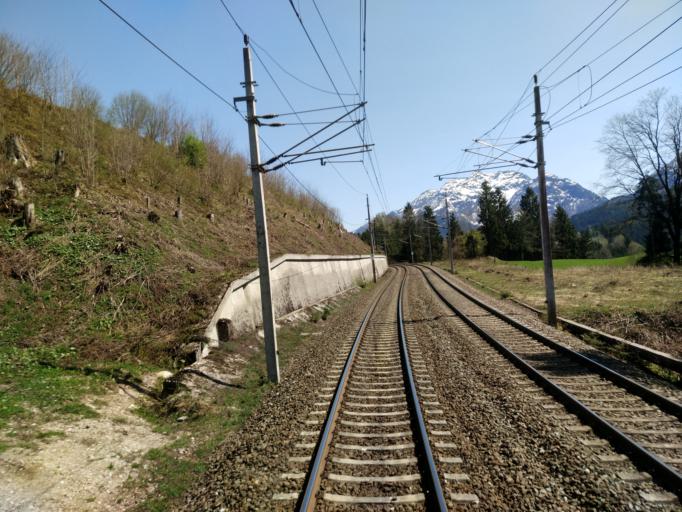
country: AT
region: Tyrol
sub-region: Politischer Bezirk Kitzbuhel
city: Fieberbrunn
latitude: 47.4748
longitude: 12.5584
